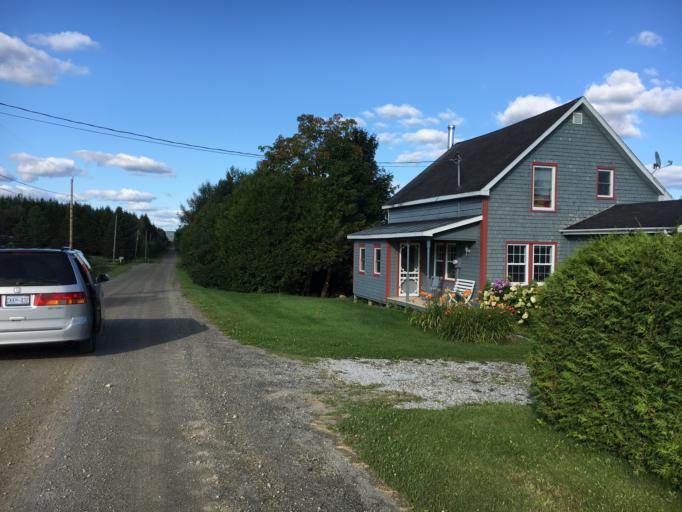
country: CA
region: Quebec
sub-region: Estrie
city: East Angus
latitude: 45.6559
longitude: -71.4143
